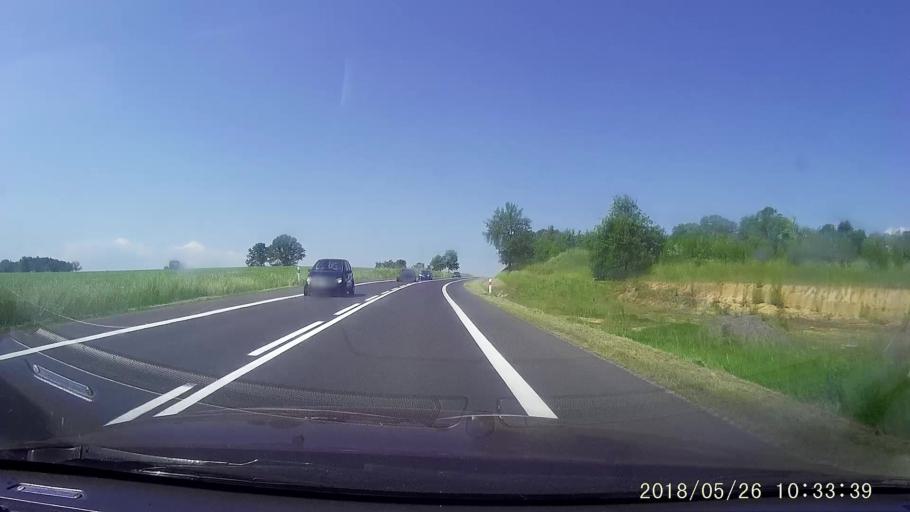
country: PL
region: Lower Silesian Voivodeship
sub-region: Powiat lubanski
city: Pisarzowice
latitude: 51.1453
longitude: 15.2074
